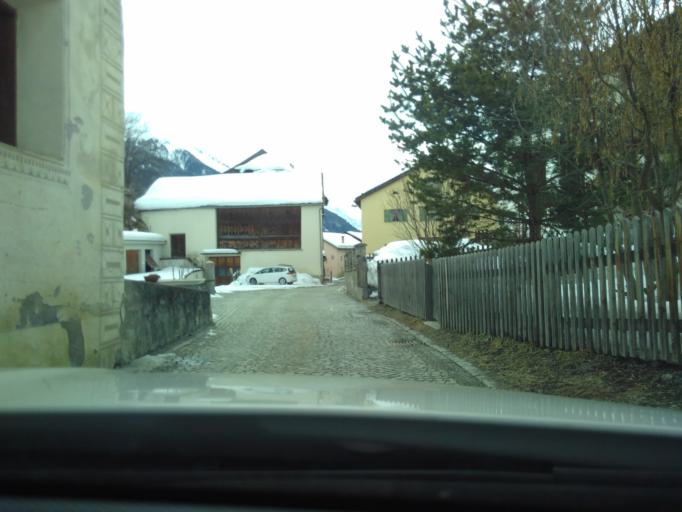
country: CH
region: Grisons
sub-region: Inn District
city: Scuol
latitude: 46.7754
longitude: 10.2051
